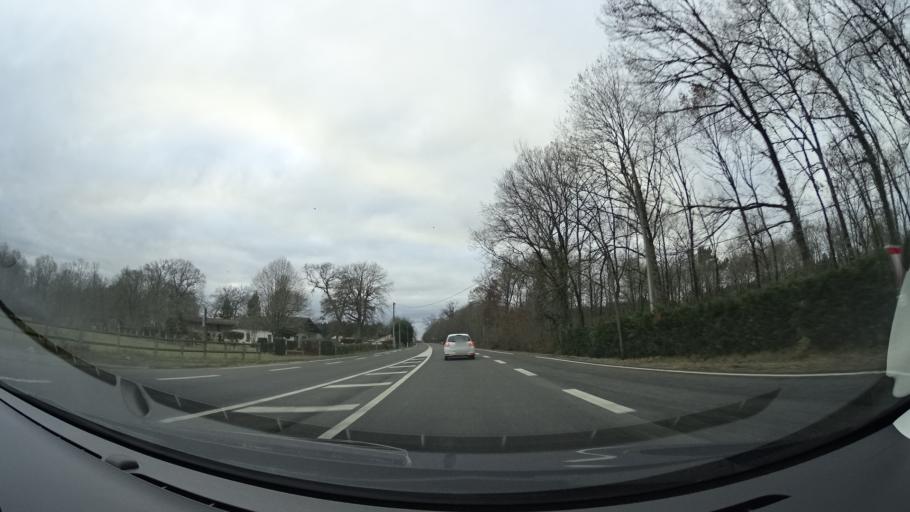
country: FR
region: Aquitaine
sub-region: Departement des Landes
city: Sarbazan
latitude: 43.9643
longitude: -0.3179
